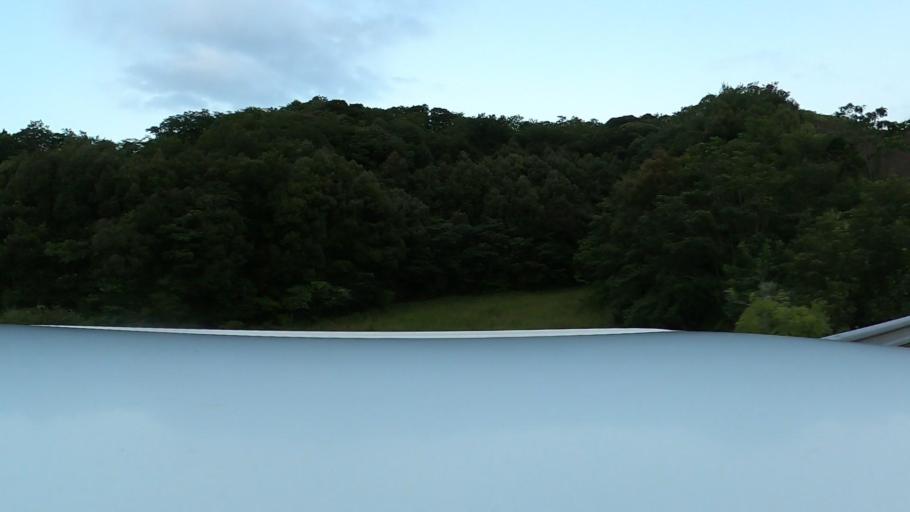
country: JP
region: Miyazaki
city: Nobeoka
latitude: 32.4583
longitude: 131.6149
